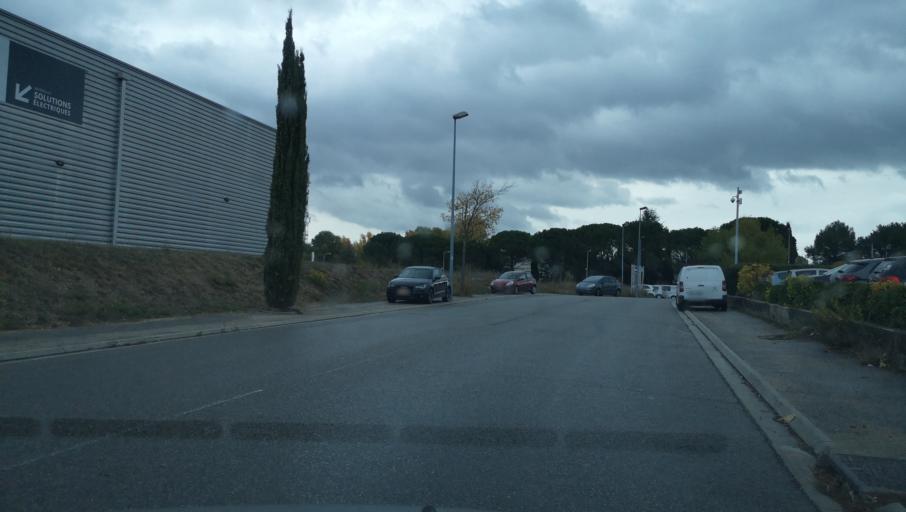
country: FR
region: Provence-Alpes-Cote d'Azur
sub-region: Departement des Bouches-du-Rhone
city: Rousset
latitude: 43.4656
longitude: 5.6102
